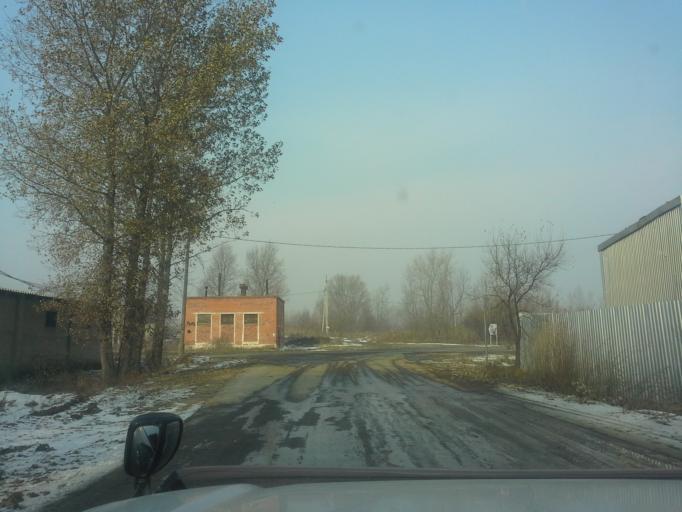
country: RU
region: Jewish Autonomous Oblast
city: Priamurskiy
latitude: 48.5351
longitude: 134.9026
